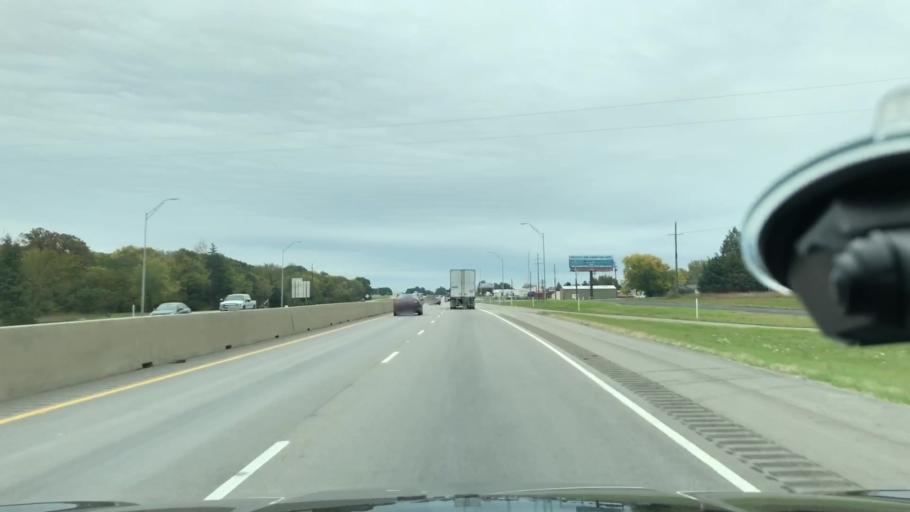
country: US
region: Texas
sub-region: Franklin County
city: Mount Vernon
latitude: 33.1617
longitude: -95.2311
